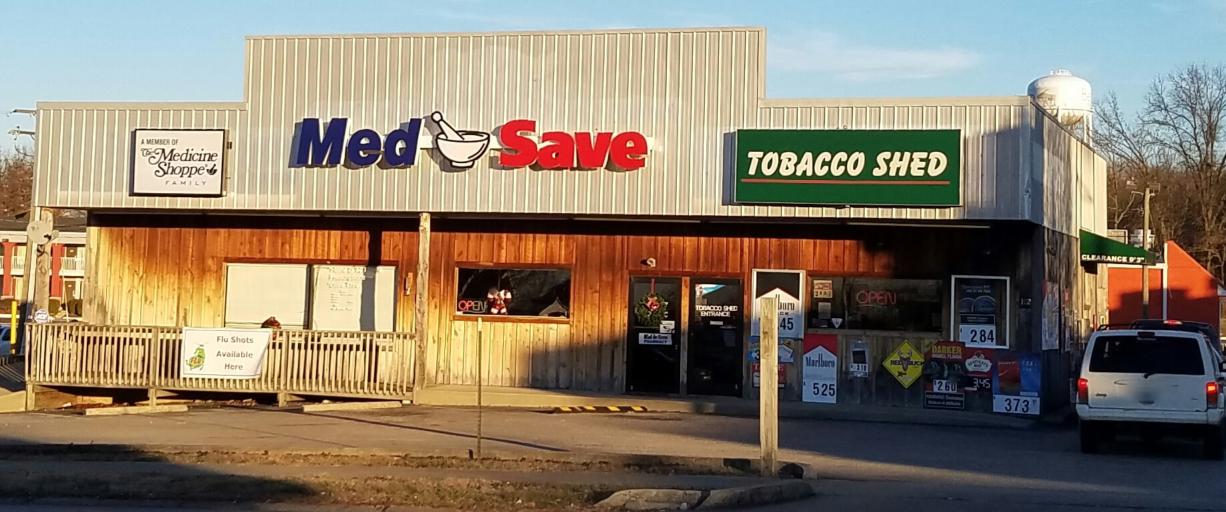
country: US
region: Kentucky
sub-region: Madison County
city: Berea
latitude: 37.5698
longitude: -84.3111
